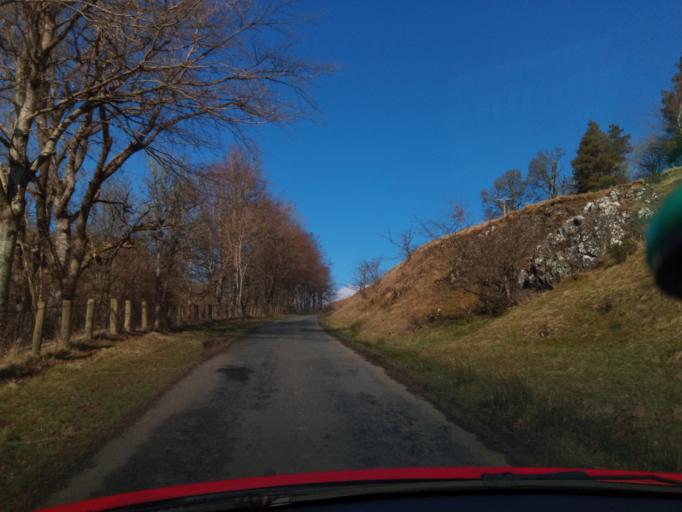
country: GB
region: Scotland
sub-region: The Scottish Borders
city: Hawick
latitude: 55.4235
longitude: -2.8725
